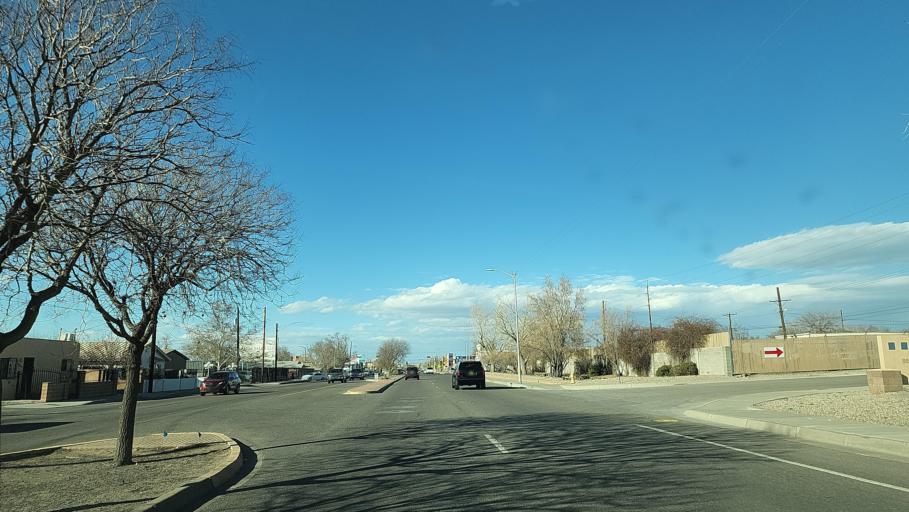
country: US
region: New Mexico
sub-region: Bernalillo County
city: Albuquerque
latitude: 35.0591
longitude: -106.6452
